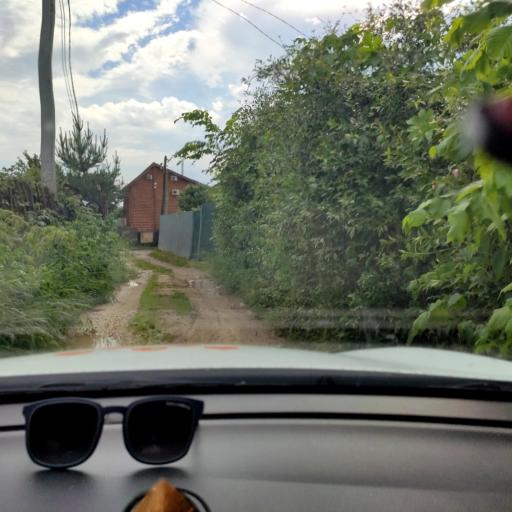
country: RU
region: Tatarstan
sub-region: Zelenodol'skiy Rayon
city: Vasil'yevo
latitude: 55.8221
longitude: 48.7305
